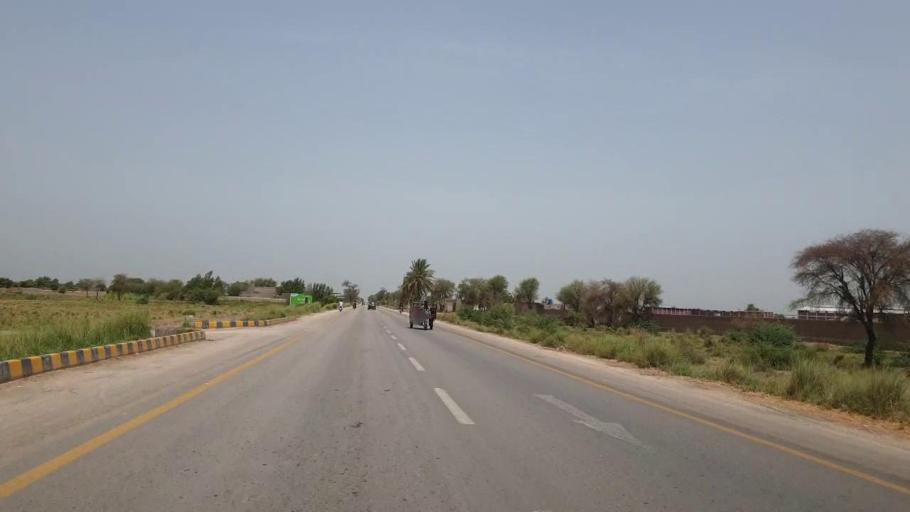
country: PK
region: Sindh
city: Nawabshah
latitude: 26.2152
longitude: 68.5080
